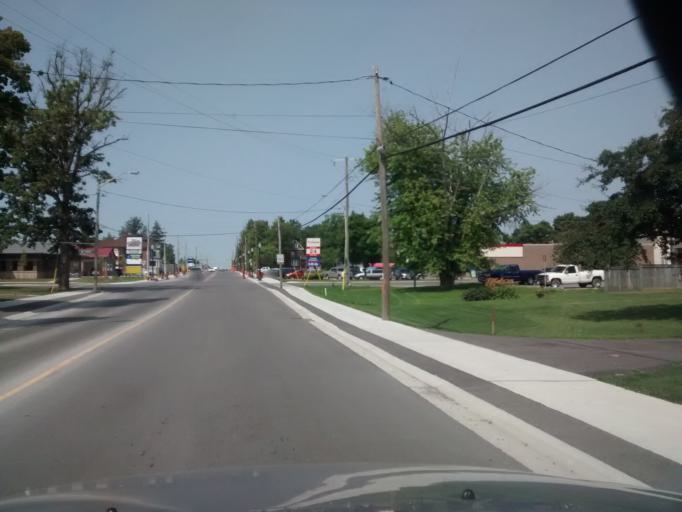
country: CA
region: Ontario
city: Hamilton
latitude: 42.9513
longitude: -79.8522
